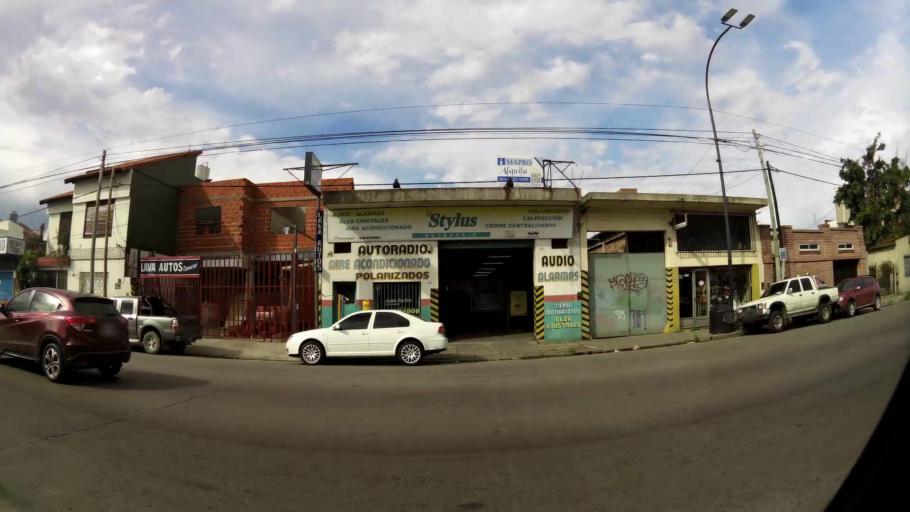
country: AR
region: Buenos Aires
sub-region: Partido de Lanus
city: Lanus
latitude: -34.6971
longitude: -58.3827
